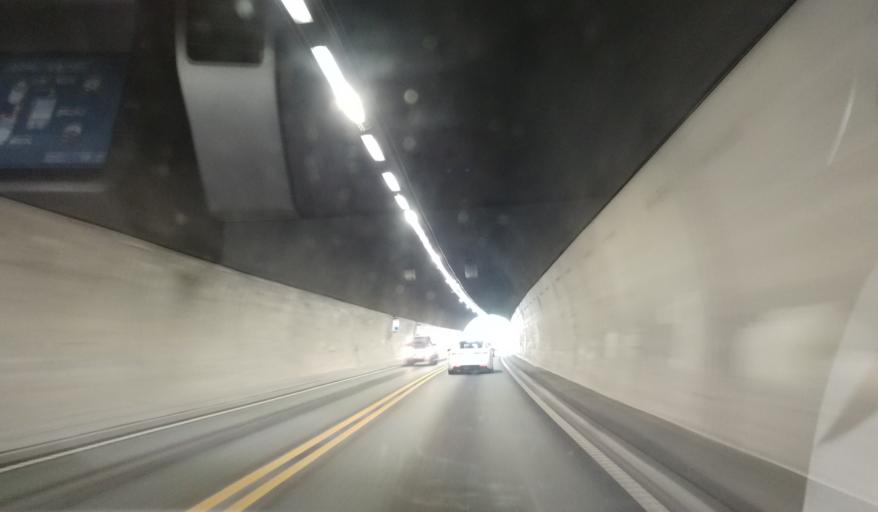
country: NO
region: Sor-Trondelag
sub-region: Malvik
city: Hommelvik
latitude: 63.4101
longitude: 10.7755
